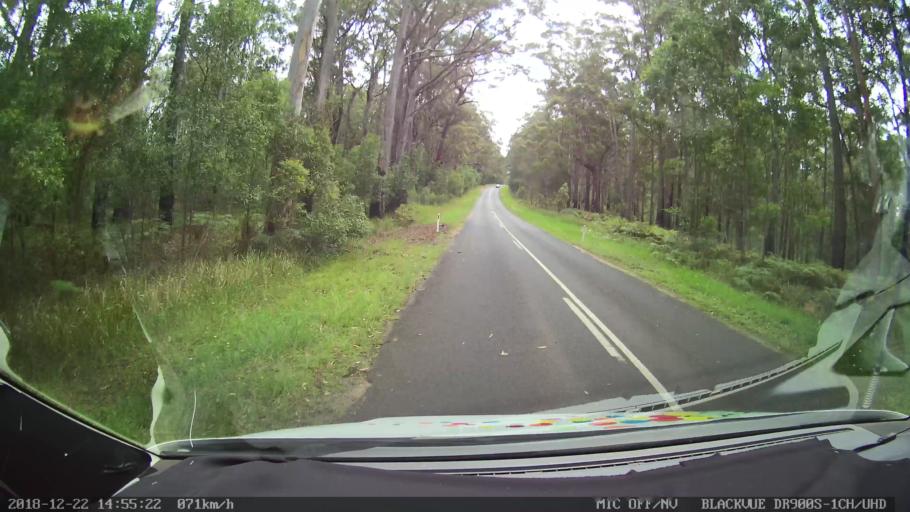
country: AU
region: New South Wales
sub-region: Bellingen
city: Dorrigo
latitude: -30.2294
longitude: 152.5223
